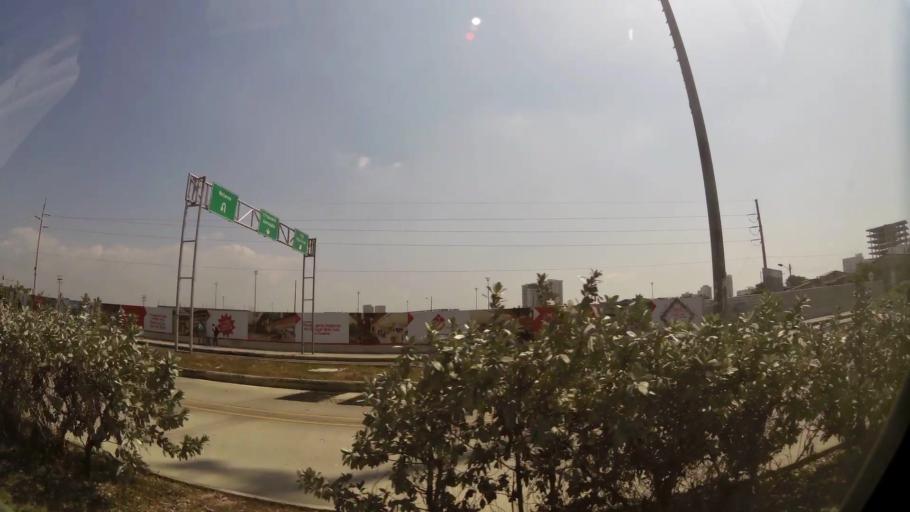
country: CO
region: Bolivar
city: Cartagena
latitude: 10.3973
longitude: -75.4736
